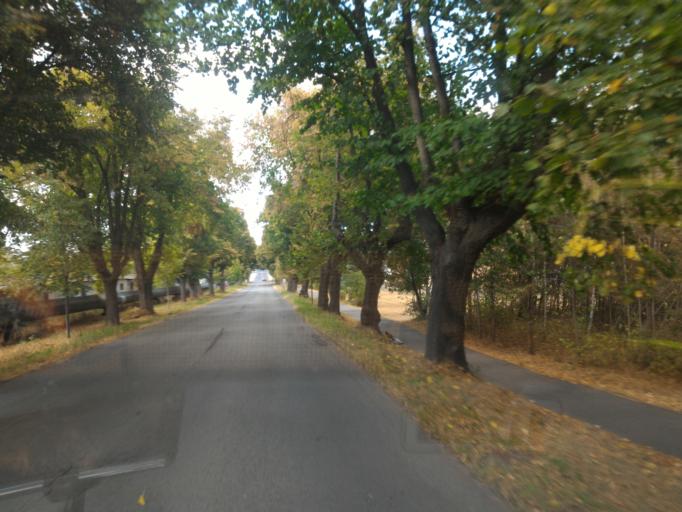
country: CZ
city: Mimon
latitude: 50.6479
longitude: 14.7376
